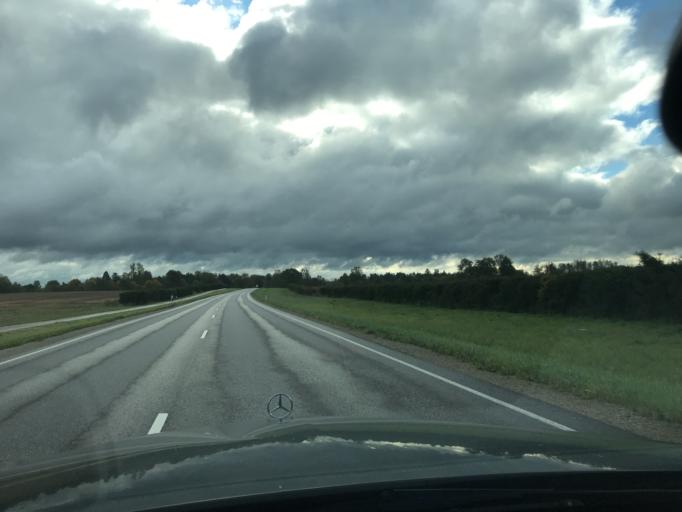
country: EE
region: Valgamaa
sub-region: Torva linn
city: Torva
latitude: 58.0232
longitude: 25.8689
